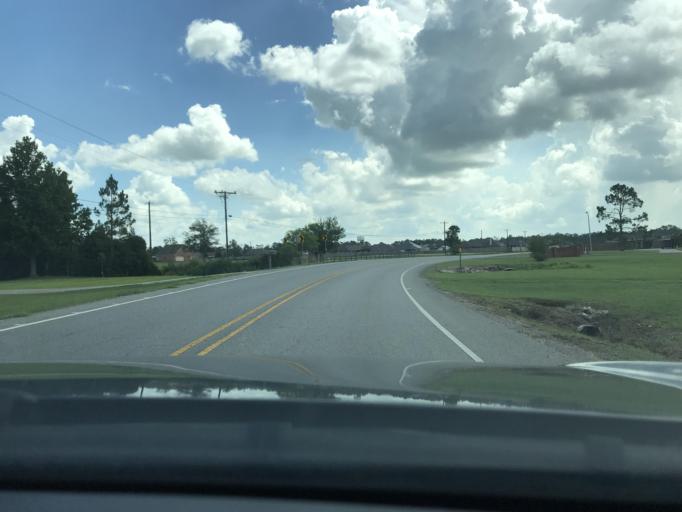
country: US
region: Louisiana
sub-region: Calcasieu Parish
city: Moss Bluff
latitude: 30.3405
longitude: -93.2440
